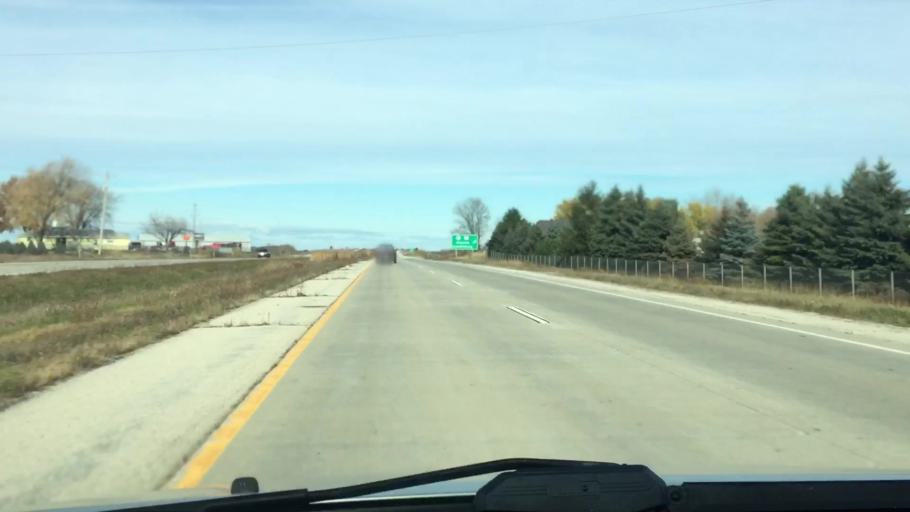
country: US
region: Wisconsin
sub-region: Brown County
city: Bellevue
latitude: 44.5328
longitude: -87.8829
